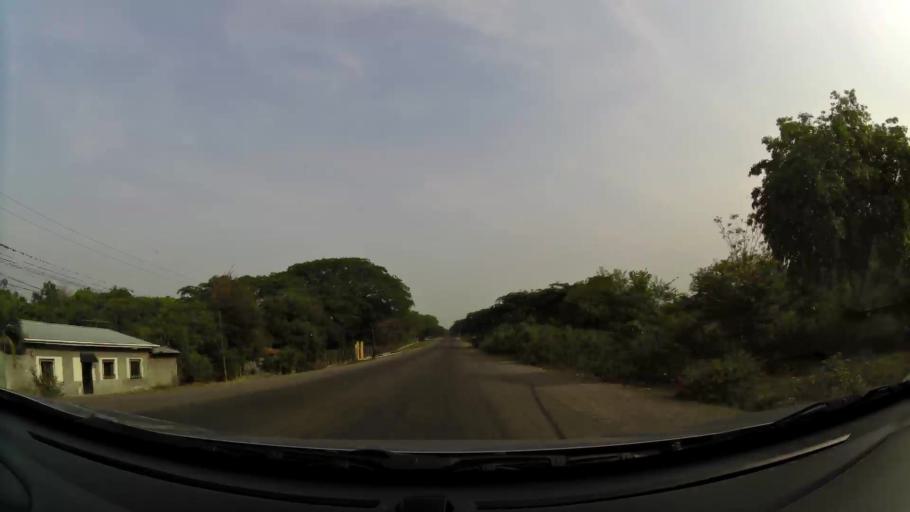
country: HN
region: Comayagua
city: Flores
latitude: 14.2769
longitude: -87.5616
